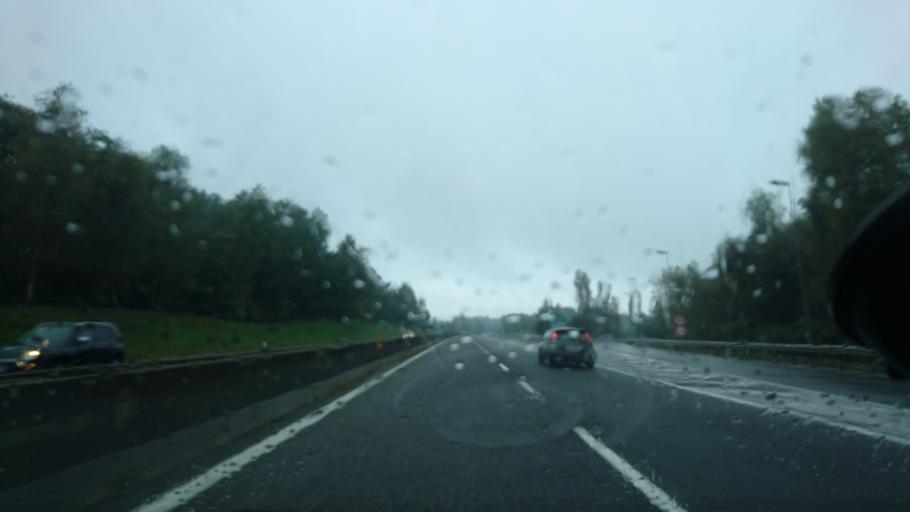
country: IT
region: Piedmont
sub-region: Provincia di Novara
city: Paruzzaro
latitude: 45.7285
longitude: 8.5150
